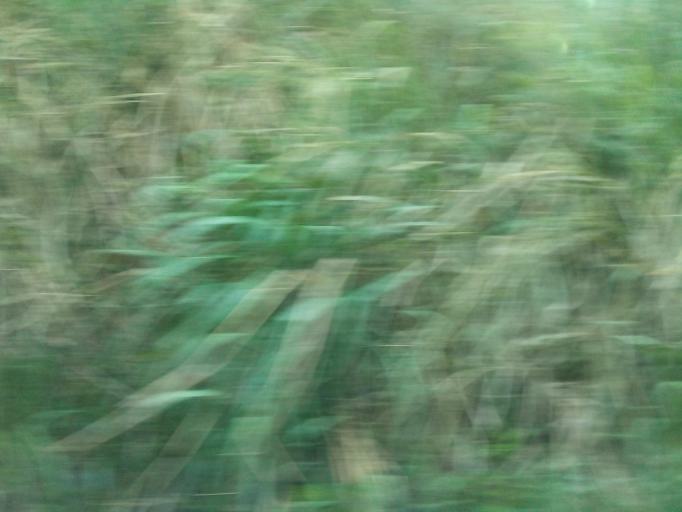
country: BR
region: Minas Gerais
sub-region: Belo Horizonte
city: Belo Horizonte
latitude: -19.8796
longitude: -43.8601
